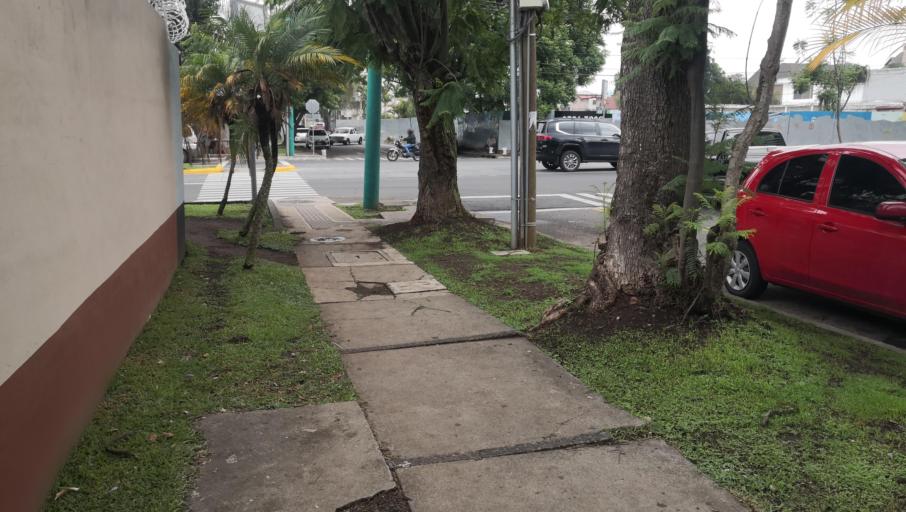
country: GT
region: Guatemala
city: Santa Catarina Pinula
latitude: 14.5817
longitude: -90.5235
